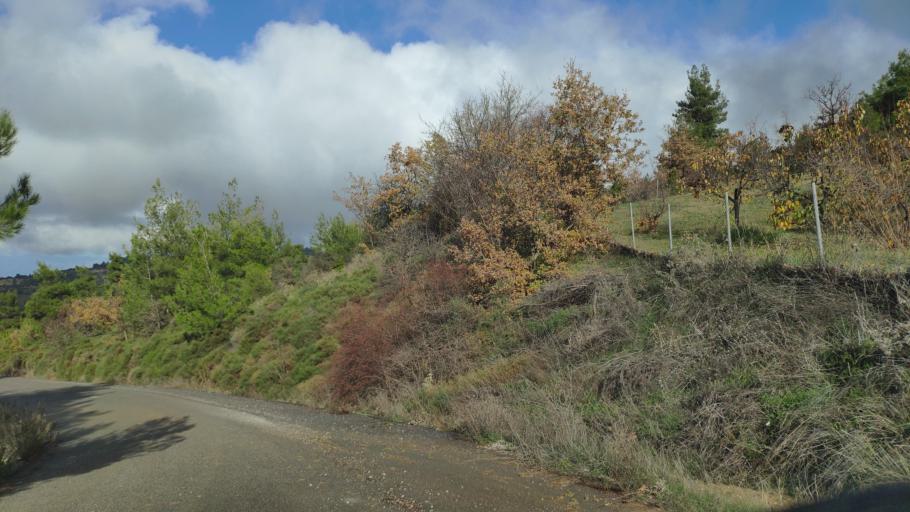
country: GR
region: West Greece
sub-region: Nomos Achaias
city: Aiyira
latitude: 38.0745
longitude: 22.4684
